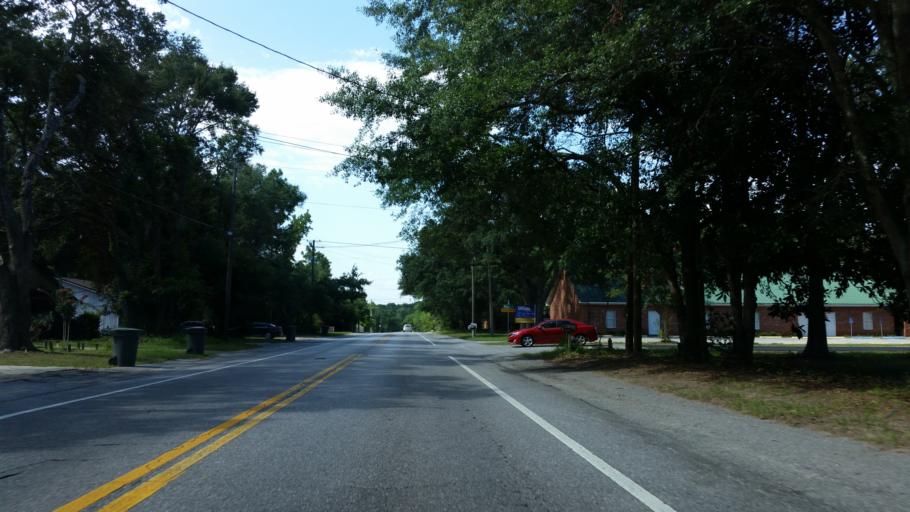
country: US
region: Florida
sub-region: Escambia County
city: Ensley
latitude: 30.5417
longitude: -87.2474
